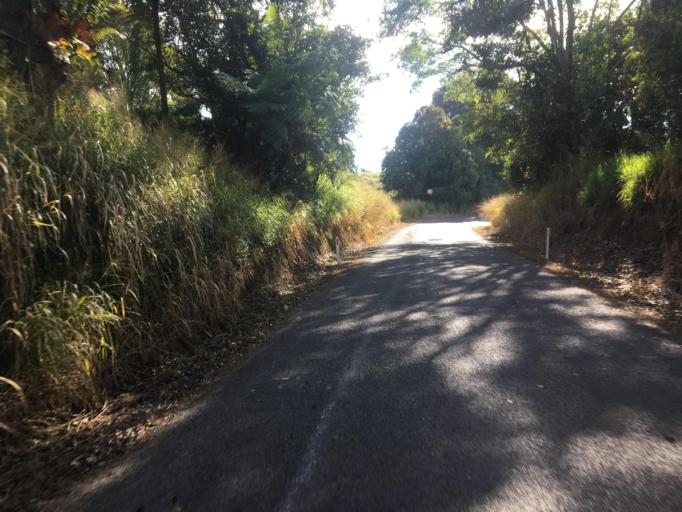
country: AU
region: Queensland
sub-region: Tablelands
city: Ravenshoe
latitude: -17.5210
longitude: 145.6088
